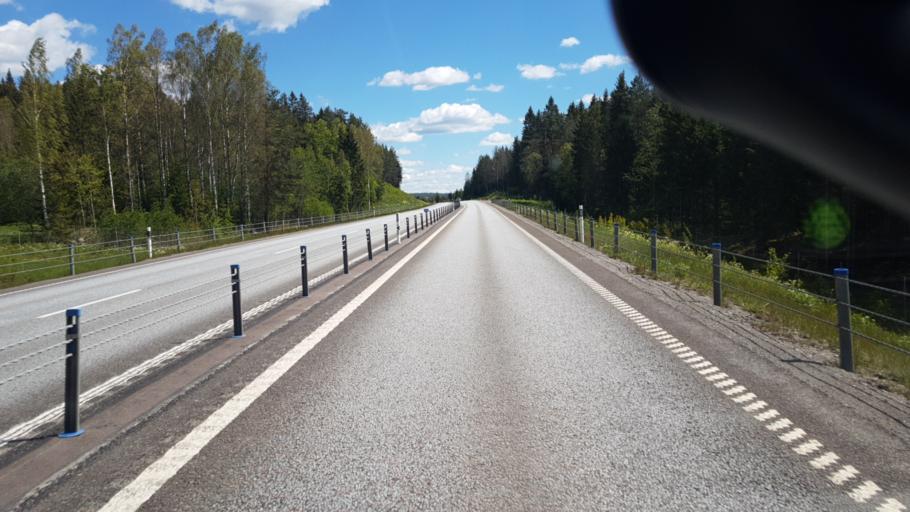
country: SE
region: Vaermland
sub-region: Arvika Kommun
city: Arvika
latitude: 59.6449
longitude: 12.7227
